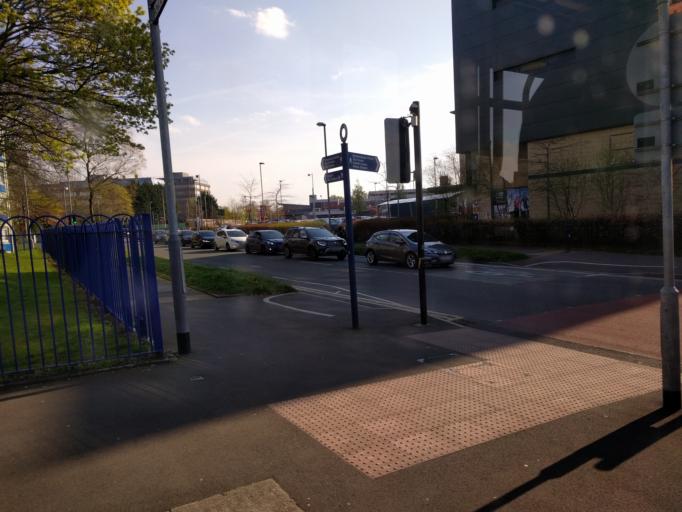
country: GB
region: England
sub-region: Manchester
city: Ringway
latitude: 53.3818
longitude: -2.2602
